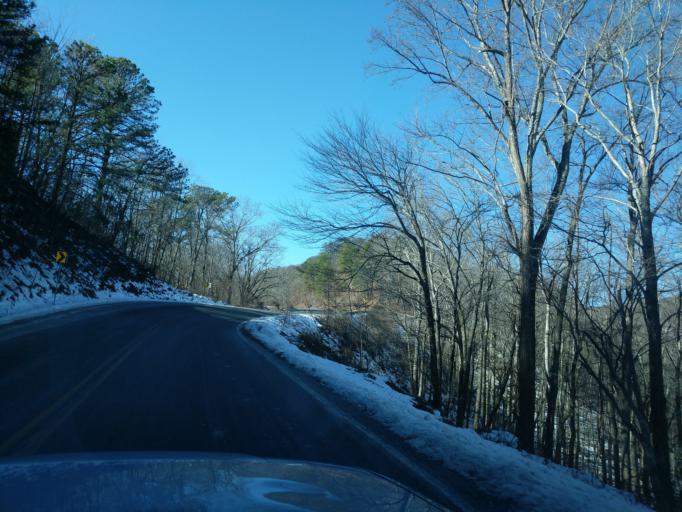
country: US
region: Georgia
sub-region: Towns County
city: Hiawassee
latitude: 34.8916
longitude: -83.5855
